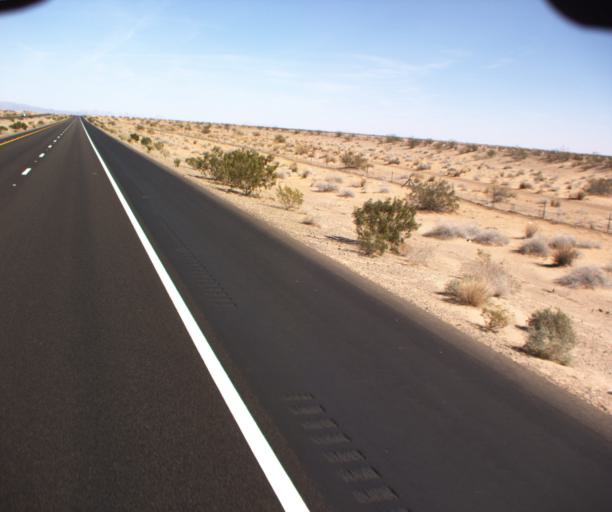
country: US
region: Arizona
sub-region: Yuma County
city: Somerton
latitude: 32.4951
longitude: -114.6201
